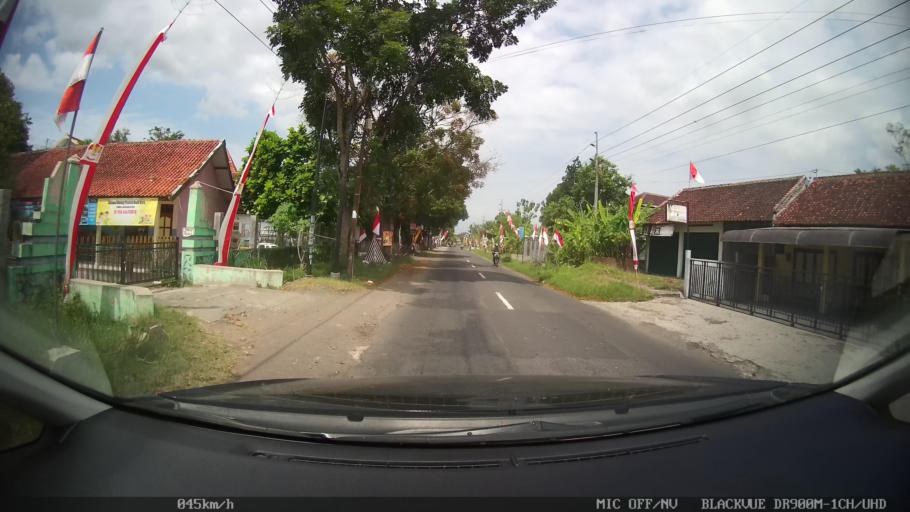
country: ID
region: Daerah Istimewa Yogyakarta
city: Depok
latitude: -7.8020
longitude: 110.4538
